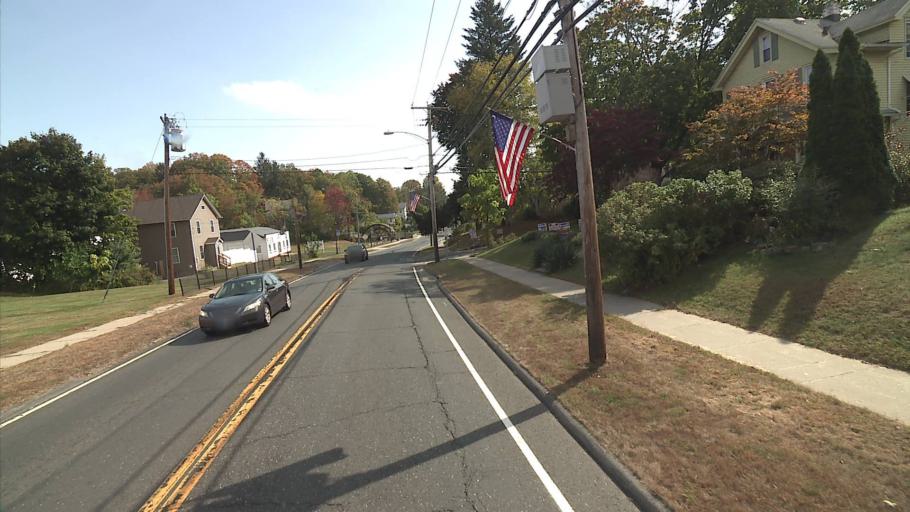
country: US
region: Connecticut
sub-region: Litchfield County
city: Terryville
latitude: 41.6803
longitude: -73.0169
